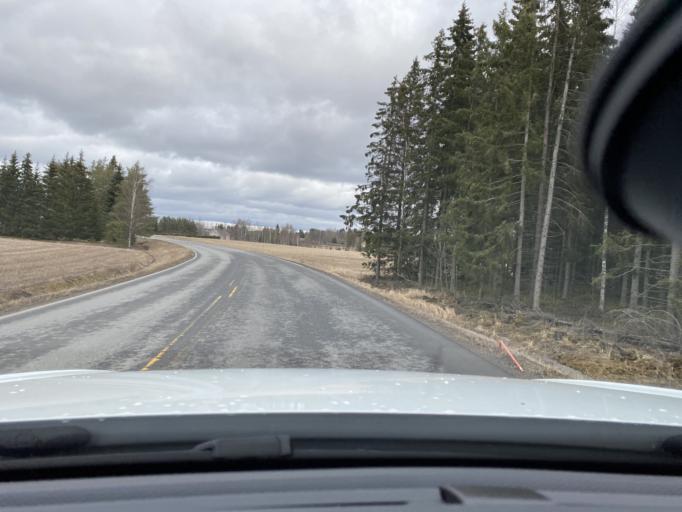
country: FI
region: Pirkanmaa
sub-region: Lounais-Pirkanmaa
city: Punkalaidun
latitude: 61.1035
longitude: 23.1813
